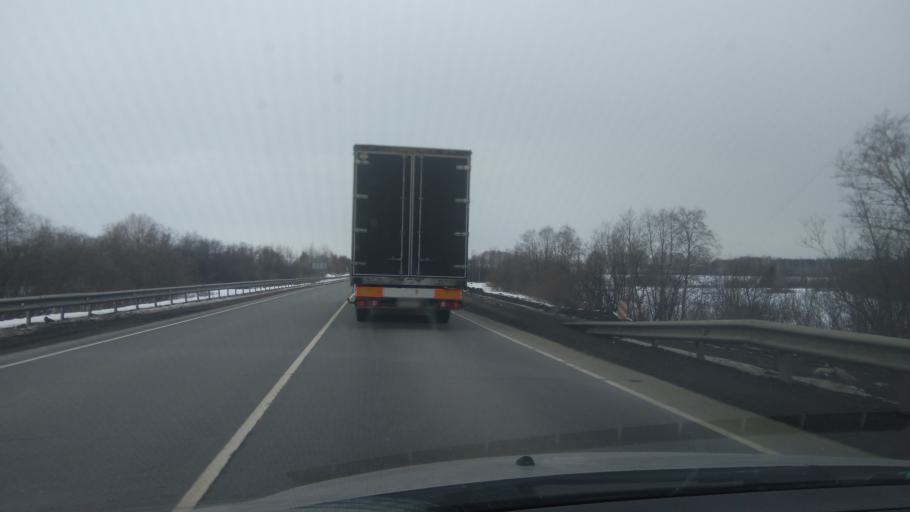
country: RU
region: Sverdlovsk
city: Ufimskiy
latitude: 56.7708
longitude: 58.0883
